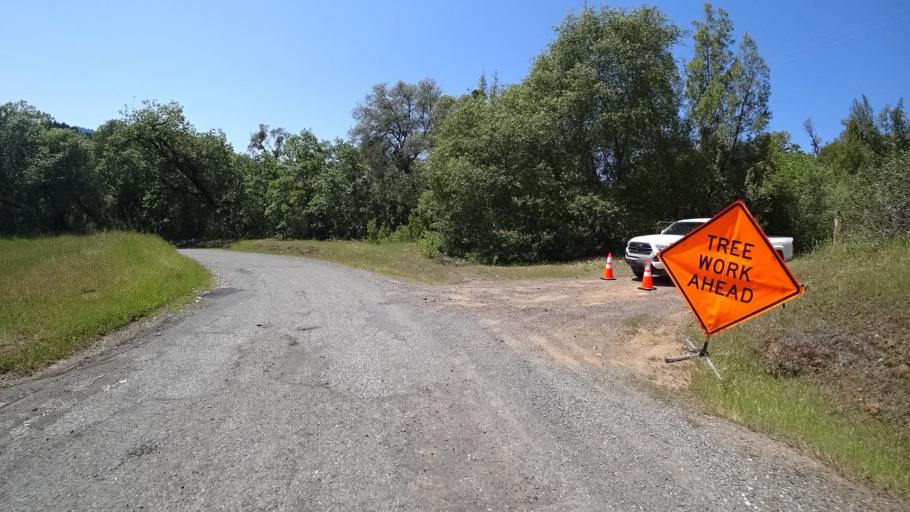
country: US
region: California
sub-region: Humboldt County
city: Redway
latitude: 40.2382
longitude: -123.6310
